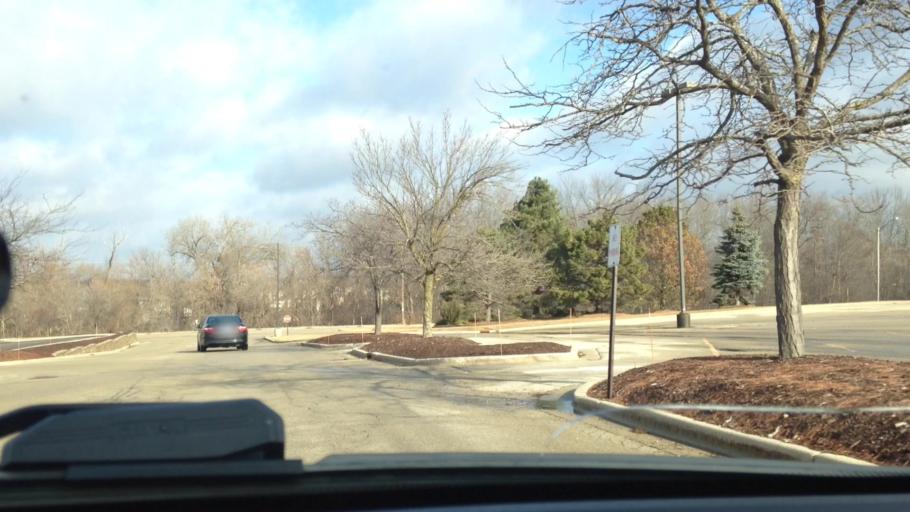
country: US
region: Wisconsin
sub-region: Waukesha County
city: Menomonee Falls
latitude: 43.1903
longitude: -88.1316
